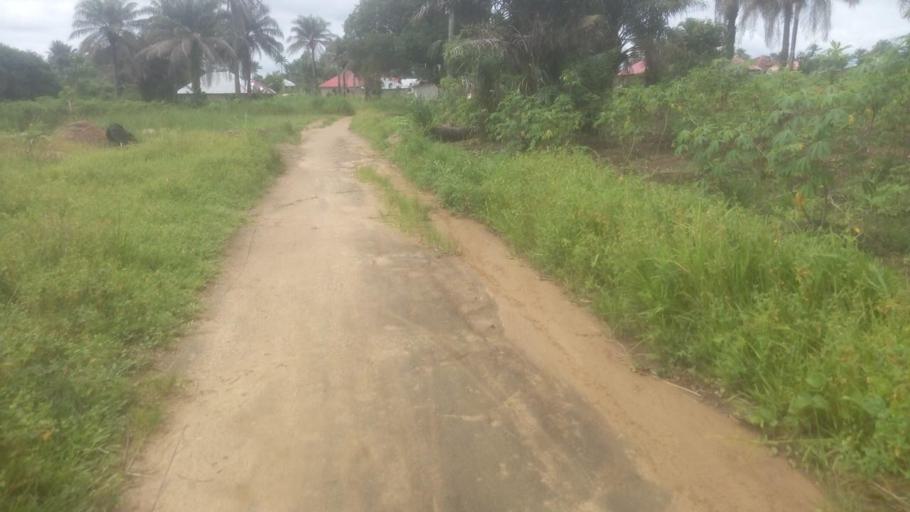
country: SL
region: Northern Province
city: Masoyila
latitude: 8.5927
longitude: -13.1859
